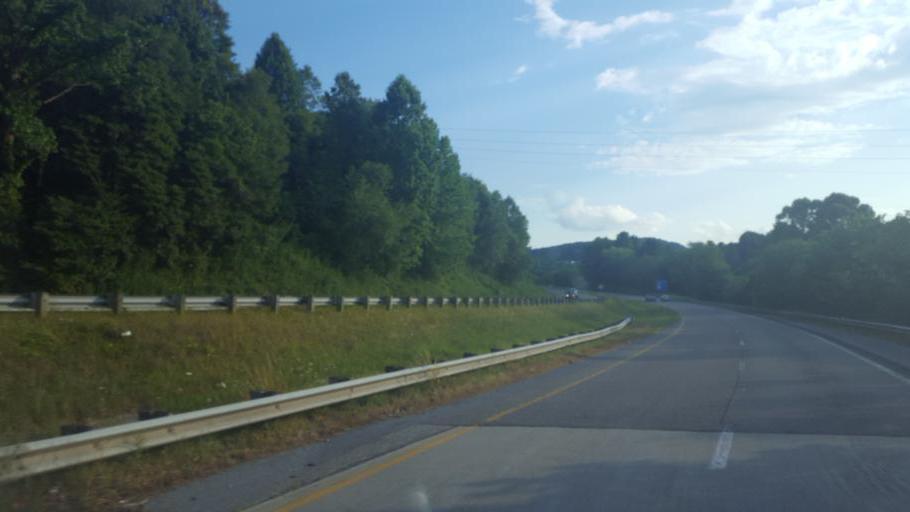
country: US
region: Virginia
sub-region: Wise County
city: Big Stone Gap
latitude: 36.8688
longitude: -82.7488
